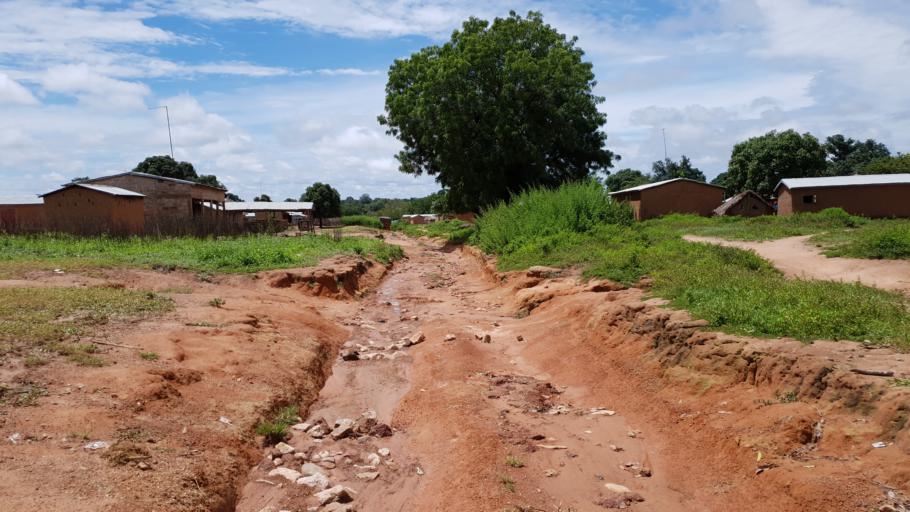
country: CI
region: Savanes
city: Tengrela
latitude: 10.3597
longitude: -6.9191
